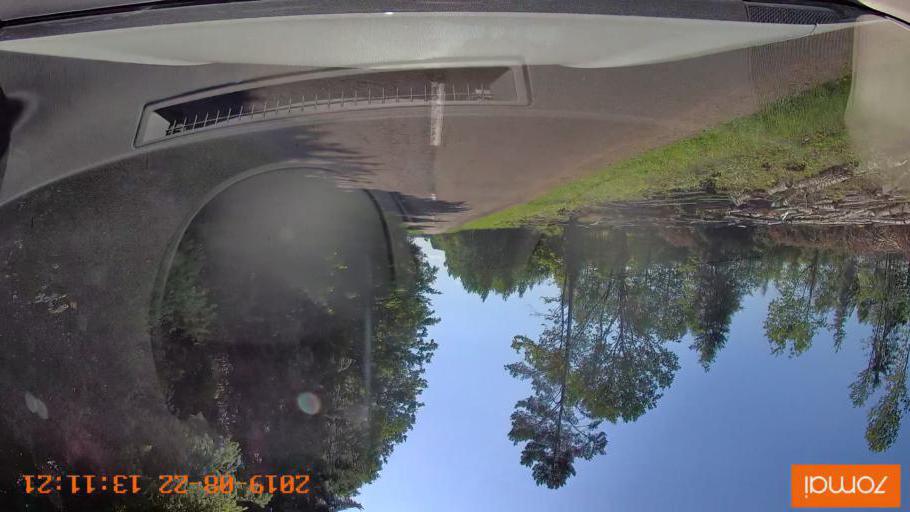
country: BY
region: Minsk
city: Prawdzinski
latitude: 53.2821
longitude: 27.8526
